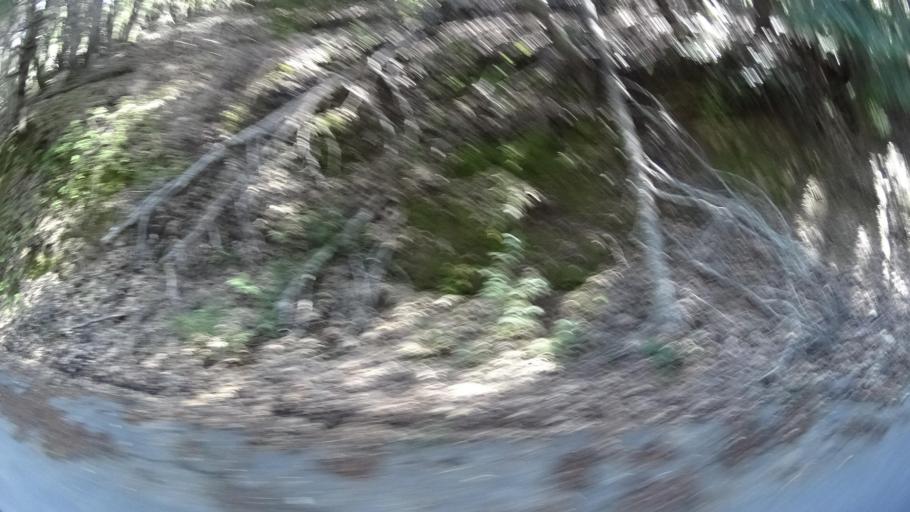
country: US
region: California
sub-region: Humboldt County
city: Redway
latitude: 40.1714
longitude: -124.0879
